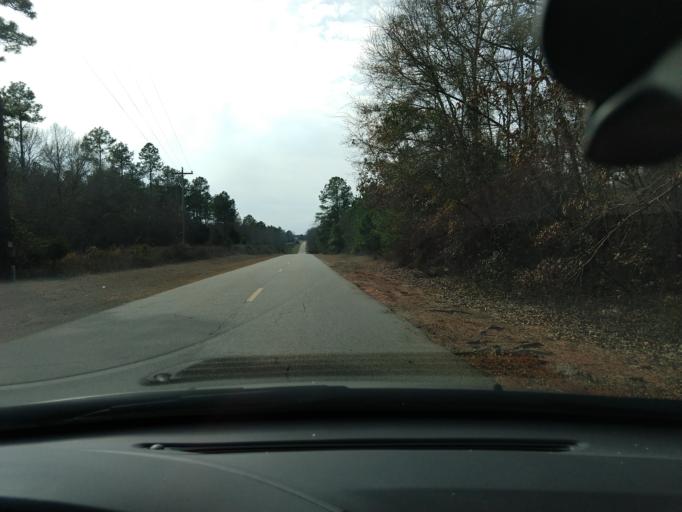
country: US
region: Georgia
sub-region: Webster County
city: Preston
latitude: 32.0319
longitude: -84.4157
